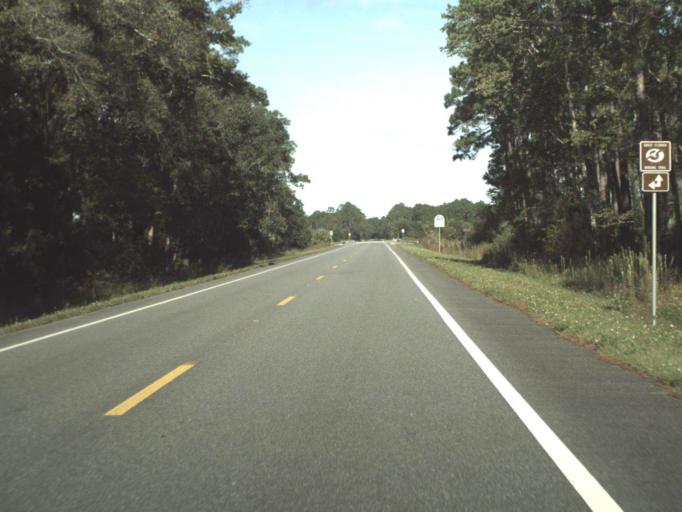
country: US
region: Florida
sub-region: Franklin County
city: Eastpoint
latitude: 29.8179
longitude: -84.8485
